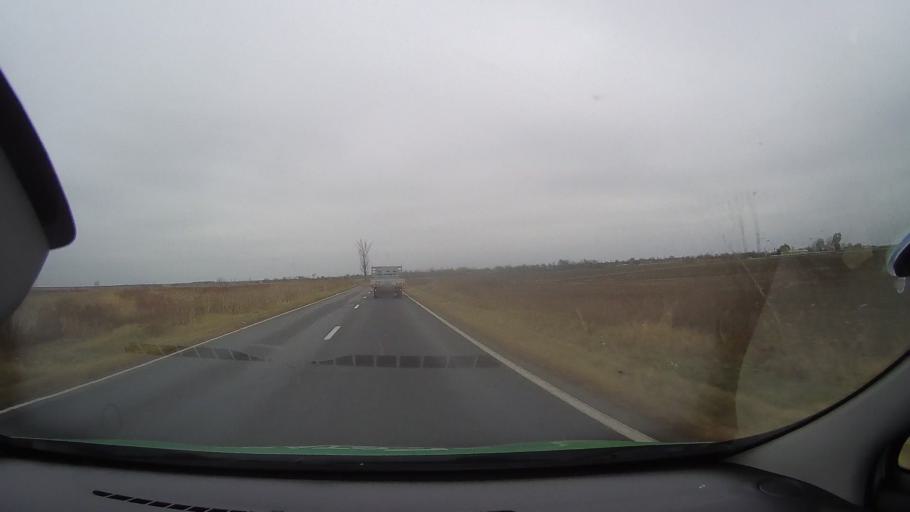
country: RO
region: Ialomita
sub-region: Comuna Scanteia
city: Iazu
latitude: 44.7352
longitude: 27.4329
